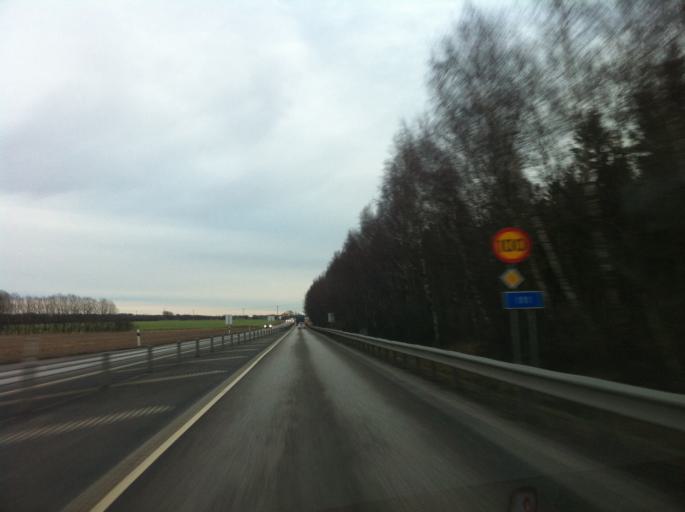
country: DK
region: Capital Region
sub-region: Helsingor Kommune
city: Hellebaek
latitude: 56.1227
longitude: 12.6195
